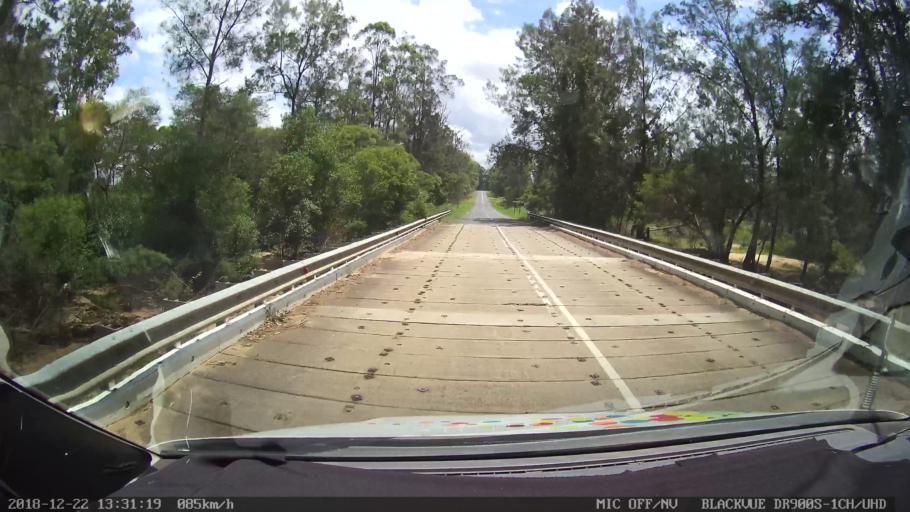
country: AU
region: New South Wales
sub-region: Clarence Valley
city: Coutts Crossing
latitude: -29.8548
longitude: 152.8543
